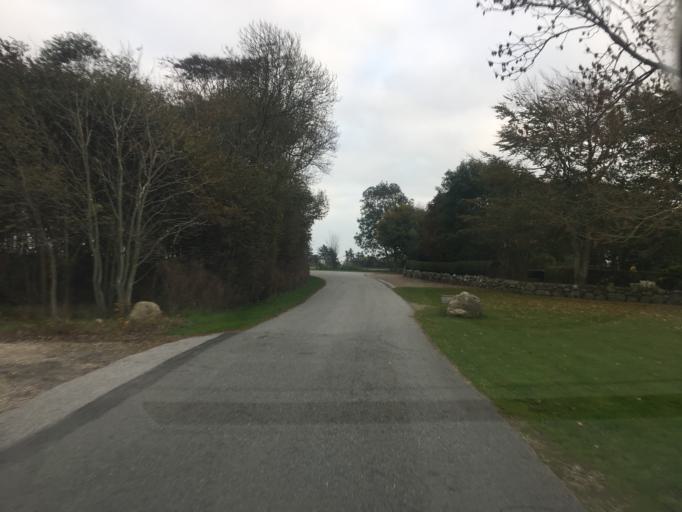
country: DE
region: Schleswig-Holstein
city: Rodenas
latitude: 54.9704
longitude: 8.7460
